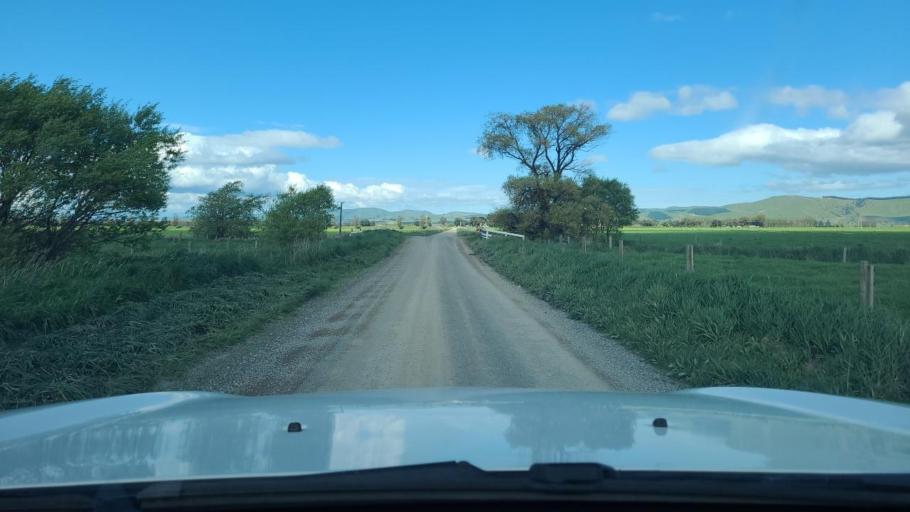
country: NZ
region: Wellington
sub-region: South Wairarapa District
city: Waipawa
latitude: -41.2406
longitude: 175.3458
